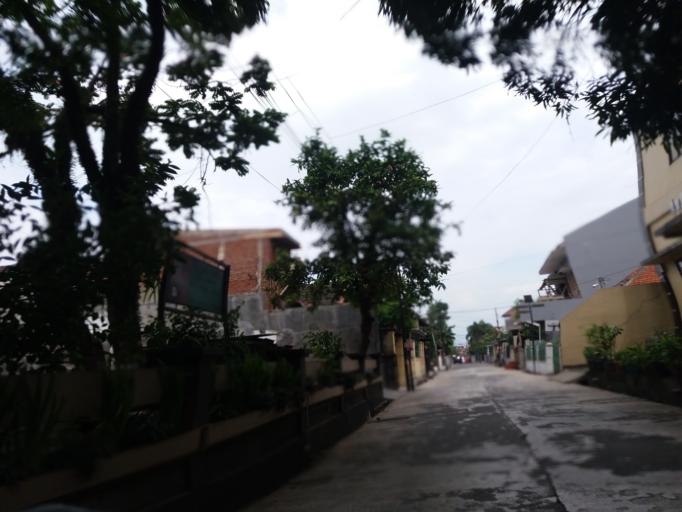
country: ID
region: West Java
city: Bandung
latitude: -6.9233
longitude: 107.6505
